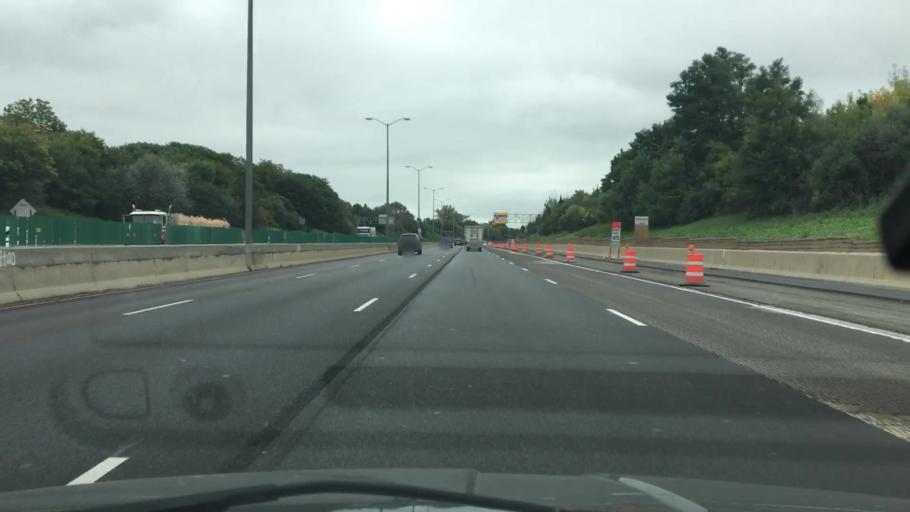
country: US
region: Illinois
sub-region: DuPage County
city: Woodridge
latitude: 41.7663
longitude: -88.0401
